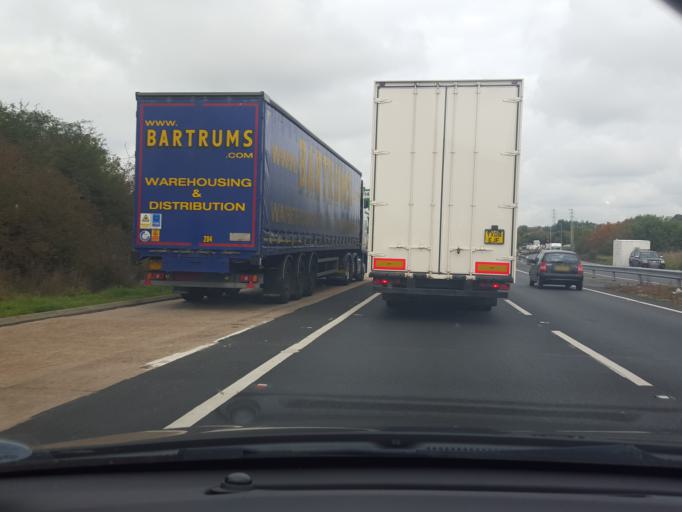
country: GB
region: England
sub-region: Suffolk
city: Bramford
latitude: 52.0323
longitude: 1.0956
